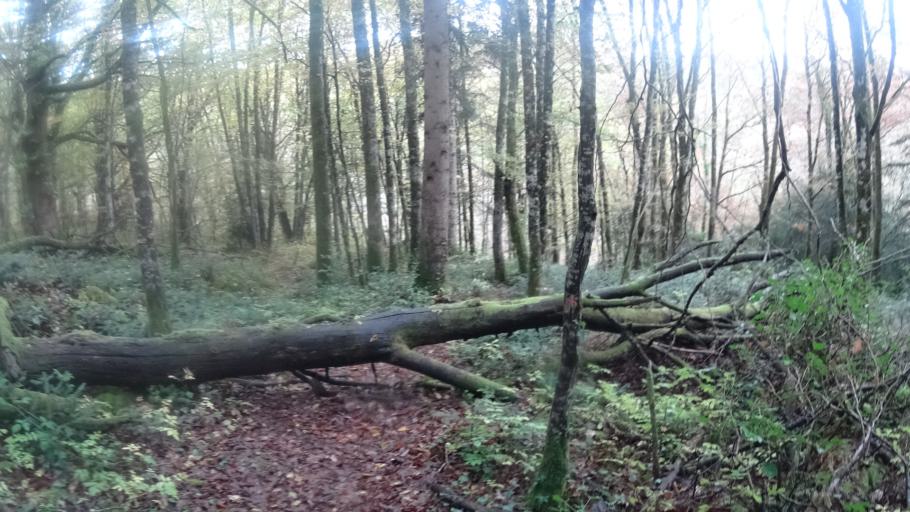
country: FR
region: Aquitaine
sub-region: Departement de la Dordogne
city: Payzac
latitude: 45.3546
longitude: 1.2044
